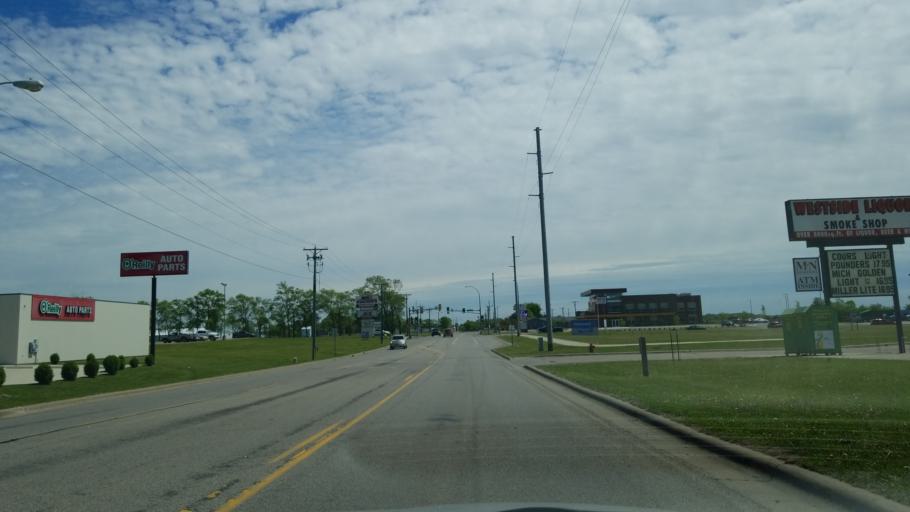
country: US
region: Minnesota
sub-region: Stearns County
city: Sauk Centre
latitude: 45.7233
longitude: -94.9492
